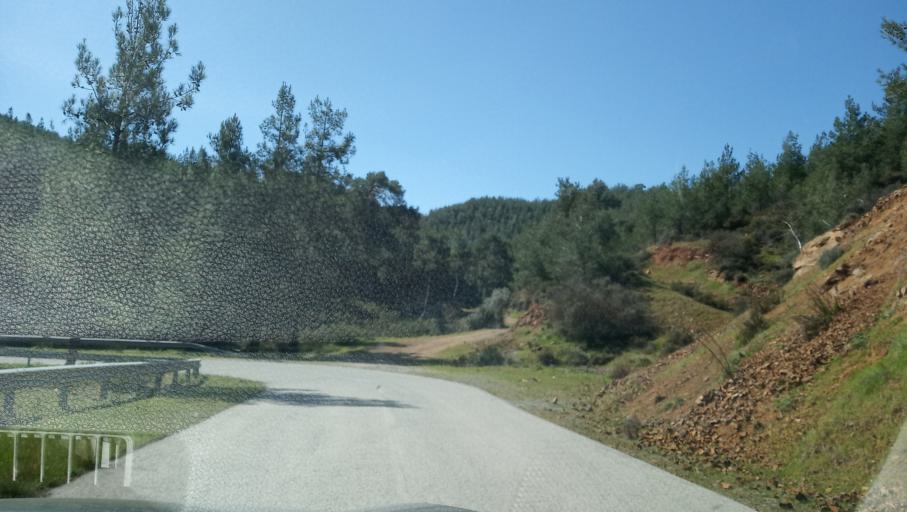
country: CY
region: Lefkosia
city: Lefka
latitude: 35.0673
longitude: 32.8150
